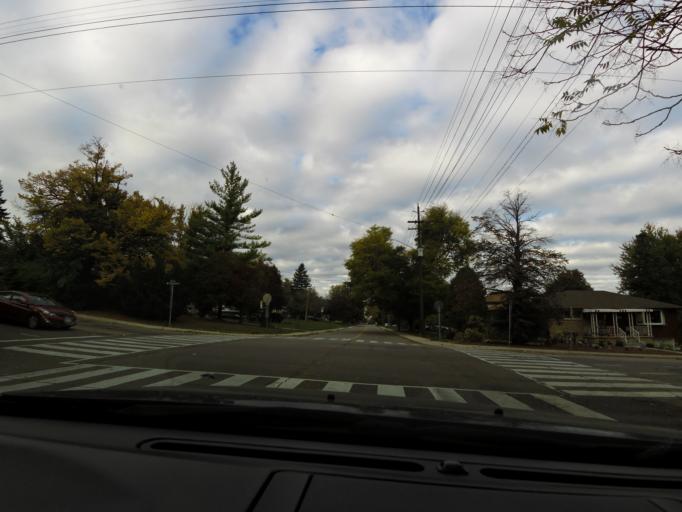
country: CA
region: Ontario
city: Hamilton
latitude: 43.2360
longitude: -79.9102
